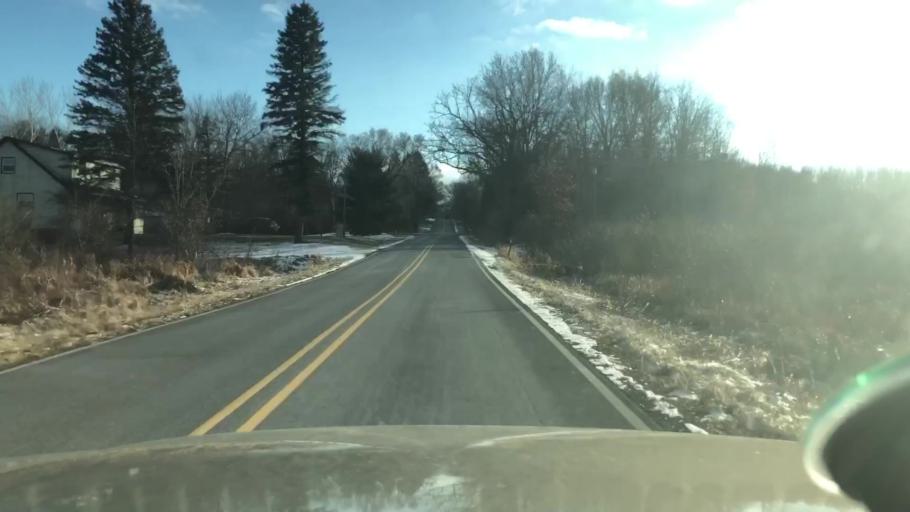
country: US
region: Michigan
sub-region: Jackson County
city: Vandercook Lake
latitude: 42.1569
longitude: -84.4521
